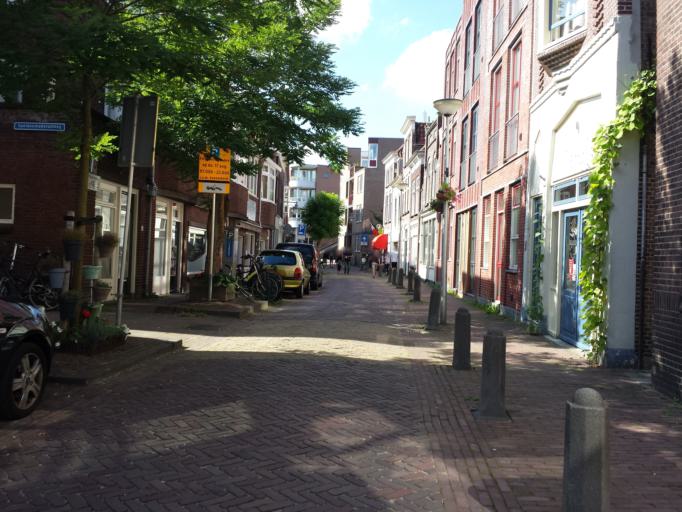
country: NL
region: South Holland
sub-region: Gemeente Gouda
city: Gouda
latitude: 52.0128
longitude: 4.7127
